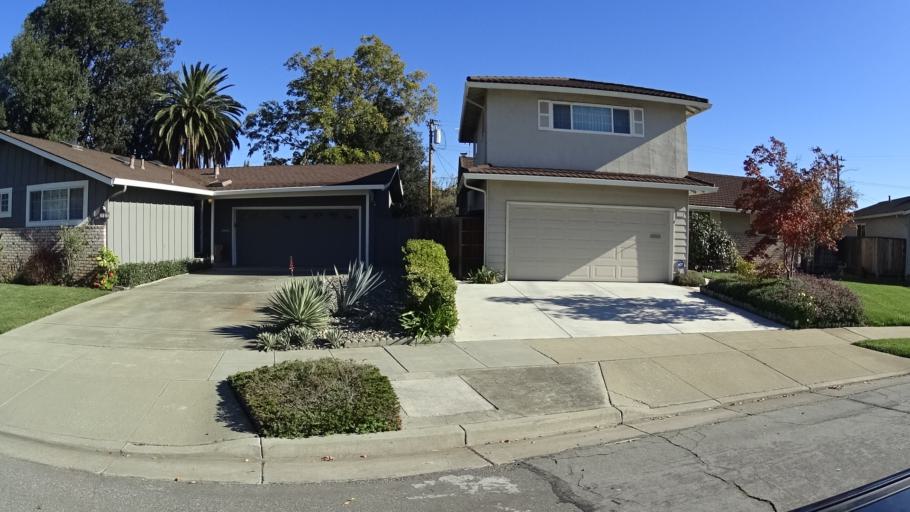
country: US
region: California
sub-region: Santa Clara County
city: Cupertino
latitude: 37.3435
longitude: -122.0118
